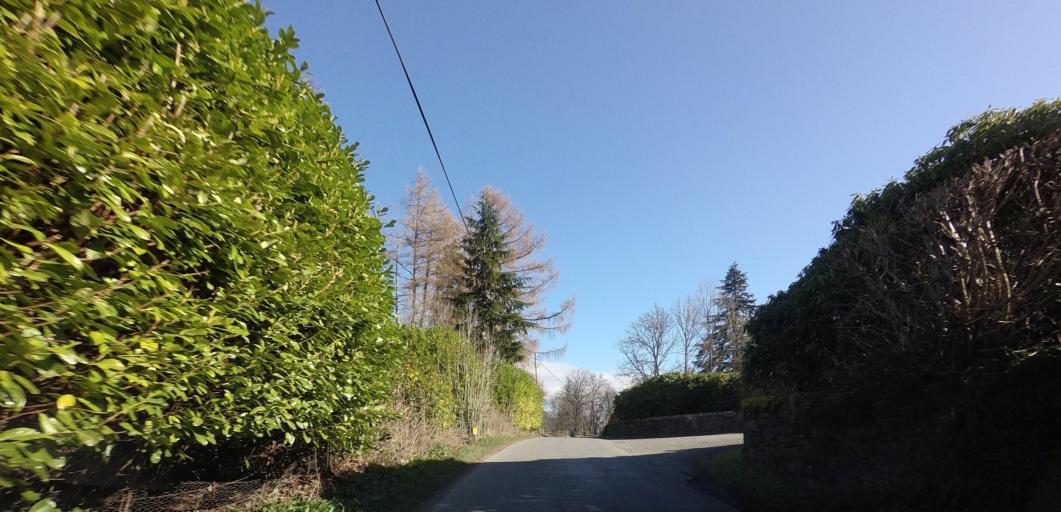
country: GB
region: Scotland
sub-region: Perth and Kinross
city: Aberfeldy
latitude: 56.5717
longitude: -4.0206
